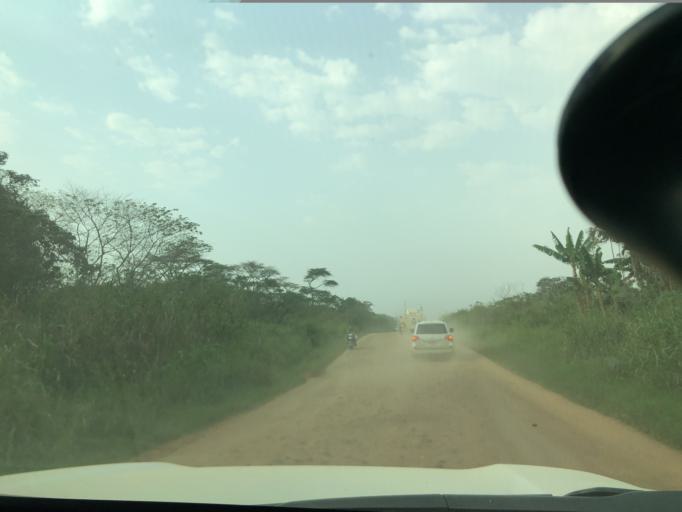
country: UG
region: Western Region
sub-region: Kasese District
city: Margherita
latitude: 0.2235
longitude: 29.6791
